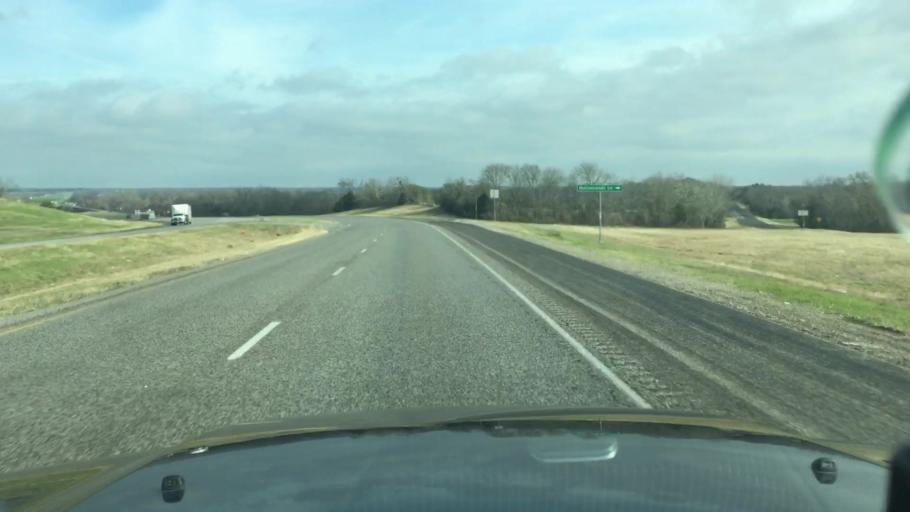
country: US
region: Texas
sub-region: Waller County
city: Hempstead
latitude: 30.1289
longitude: -96.1988
